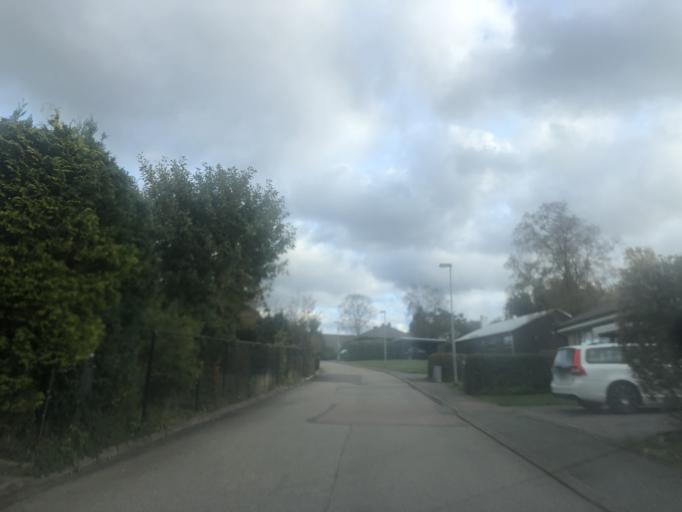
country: SE
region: Vaestra Goetaland
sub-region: Molndal
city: Moelndal
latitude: 57.6325
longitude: 11.9506
